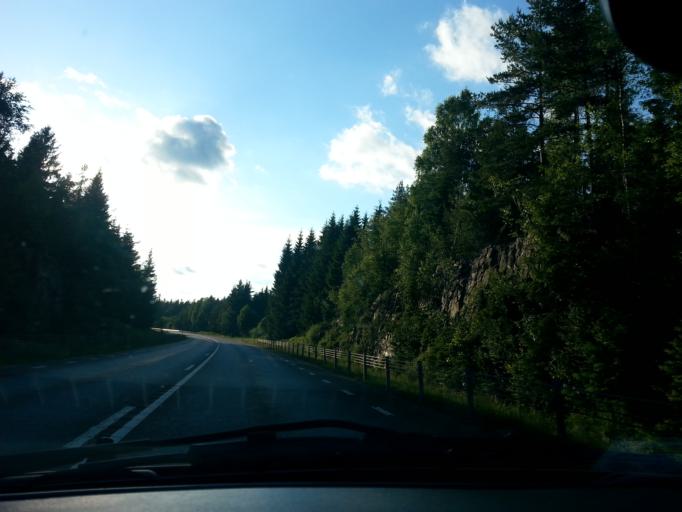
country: SE
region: Joenkoeping
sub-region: Gislaveds Kommun
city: Gislaved
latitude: 57.3356
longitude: 13.5160
